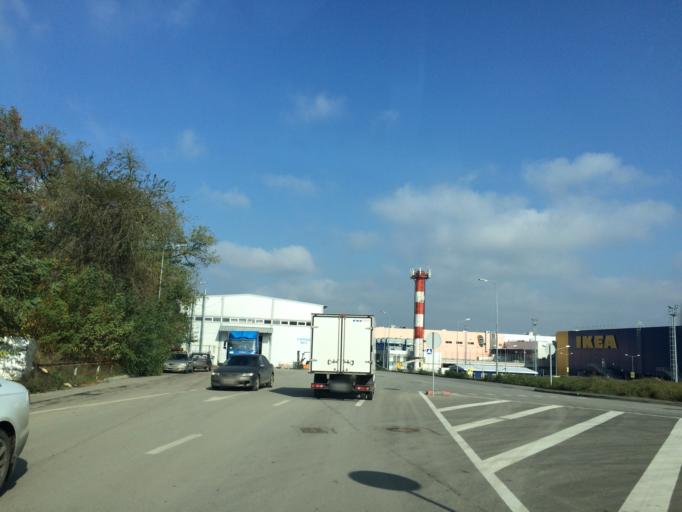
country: RU
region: Rostov
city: Aksay
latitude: 47.2868
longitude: 39.8440
